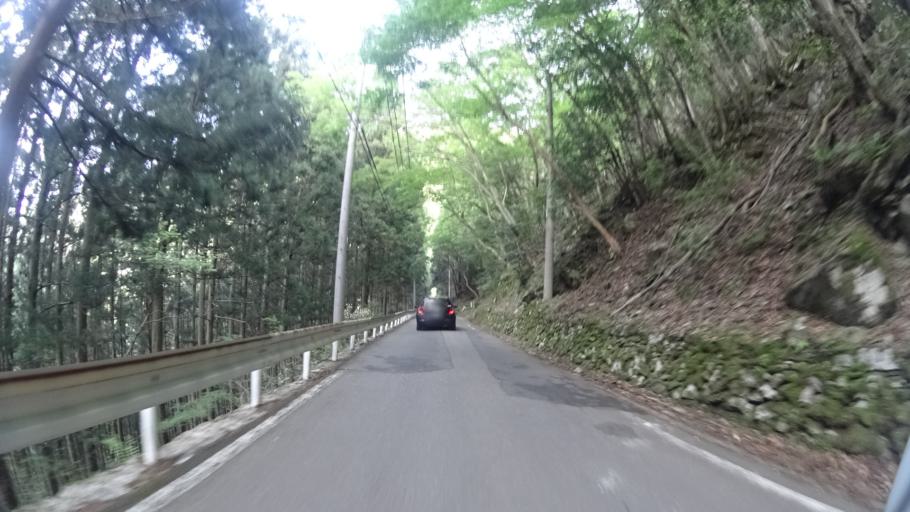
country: JP
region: Tokushima
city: Ikedacho
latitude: 33.9058
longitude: 133.8133
